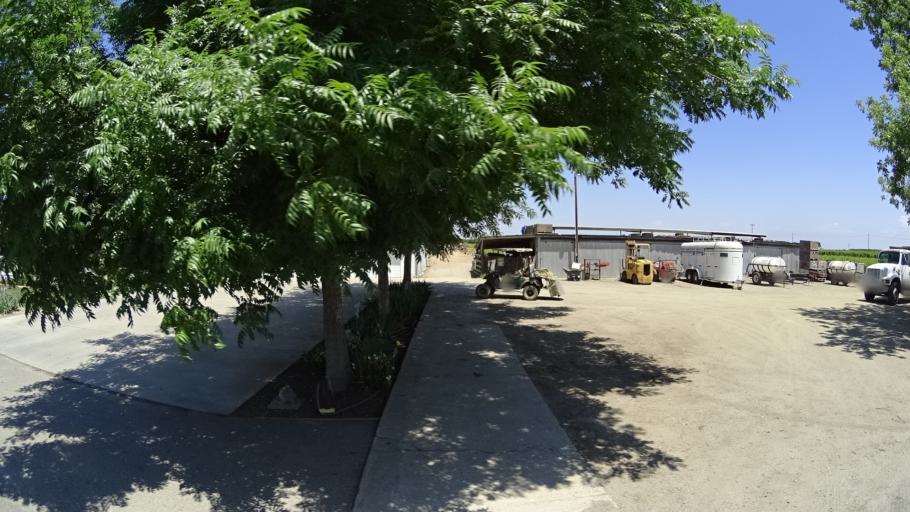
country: US
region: California
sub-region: Fresno County
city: Kingsburg
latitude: 36.4742
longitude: -119.5855
